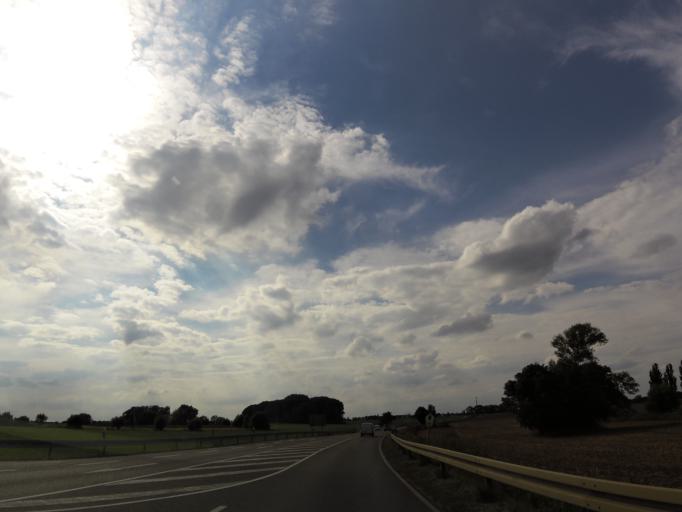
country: DE
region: Saxony
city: Markranstadt
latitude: 51.3470
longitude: 12.2456
